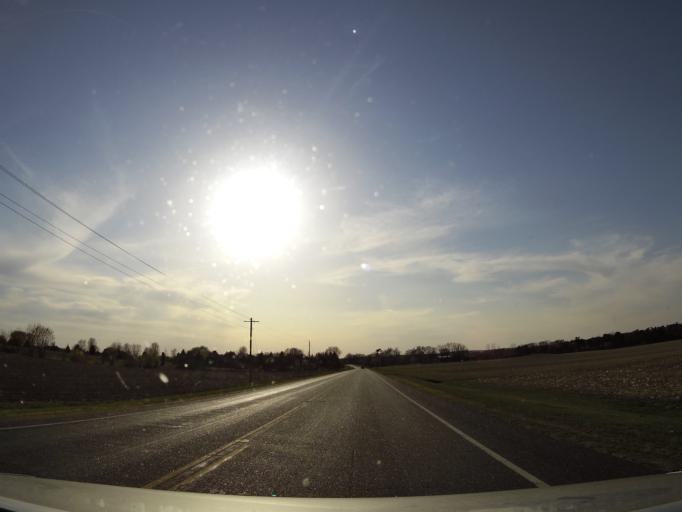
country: US
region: Minnesota
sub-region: Washington County
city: Afton
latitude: 44.8244
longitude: -92.7218
